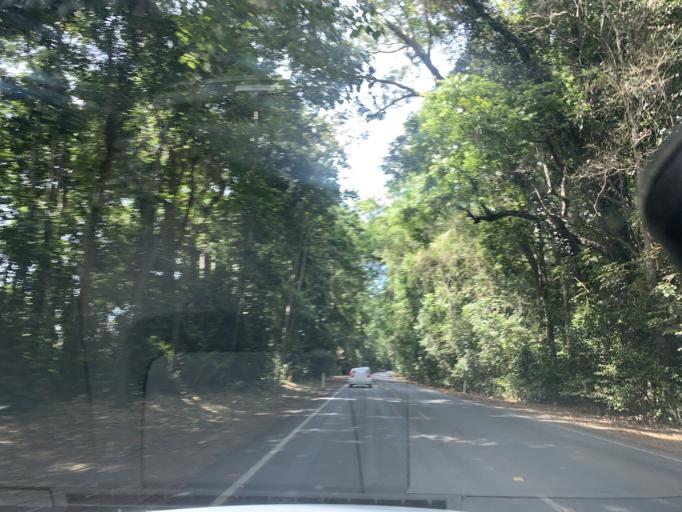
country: AU
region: Queensland
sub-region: Tablelands
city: Tolga
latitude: -17.2438
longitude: 145.4797
